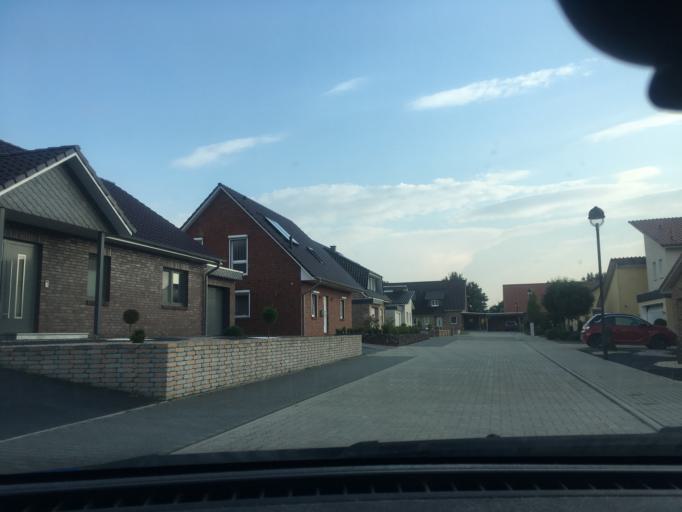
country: DE
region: Lower Saxony
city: Barendorf
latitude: 53.2275
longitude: 10.5166
